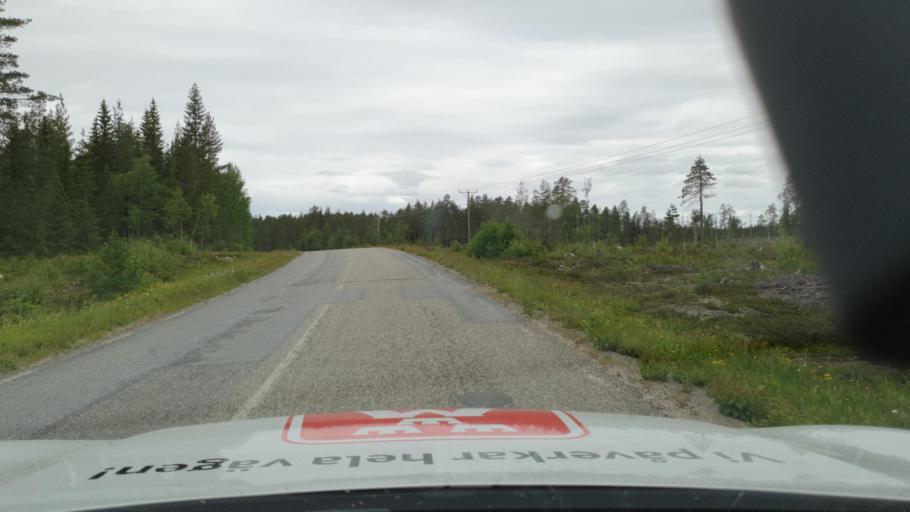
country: SE
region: Vaesterbotten
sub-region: Nordmalings Kommun
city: Nordmaling
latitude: 63.7724
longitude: 19.4175
